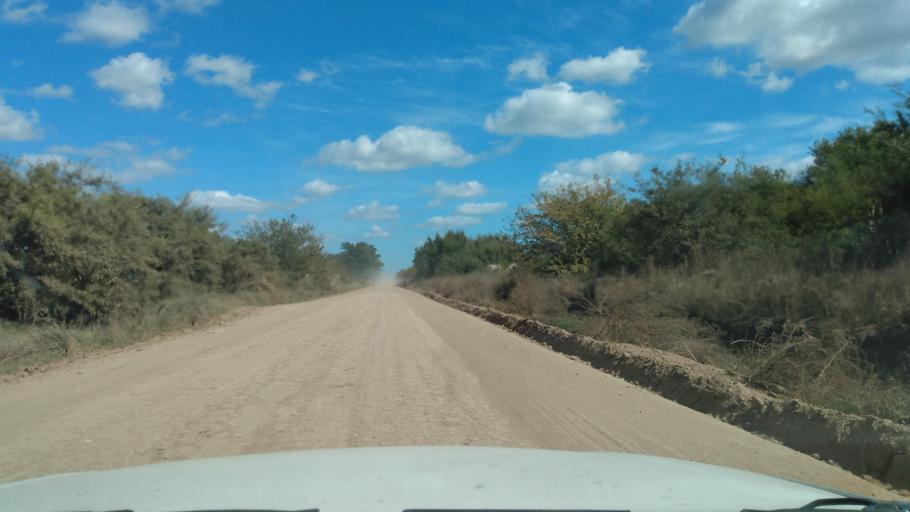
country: AR
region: Buenos Aires
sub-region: Partido de Navarro
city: Navarro
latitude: -35.0219
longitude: -59.4329
